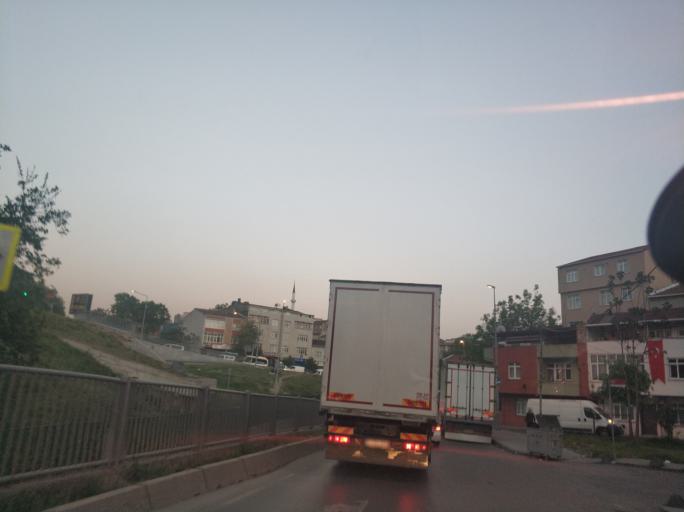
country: TR
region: Istanbul
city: Bagcilar
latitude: 41.0560
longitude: 28.8481
